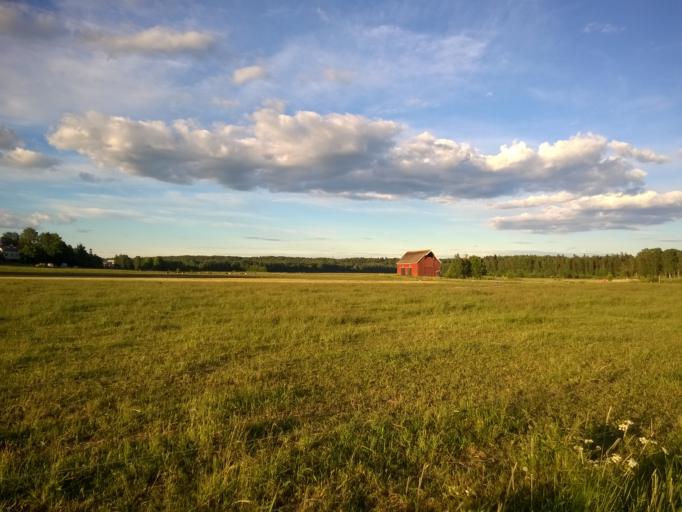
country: FI
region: Uusimaa
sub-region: Helsinki
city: Vantaa
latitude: 60.2187
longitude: 25.0124
